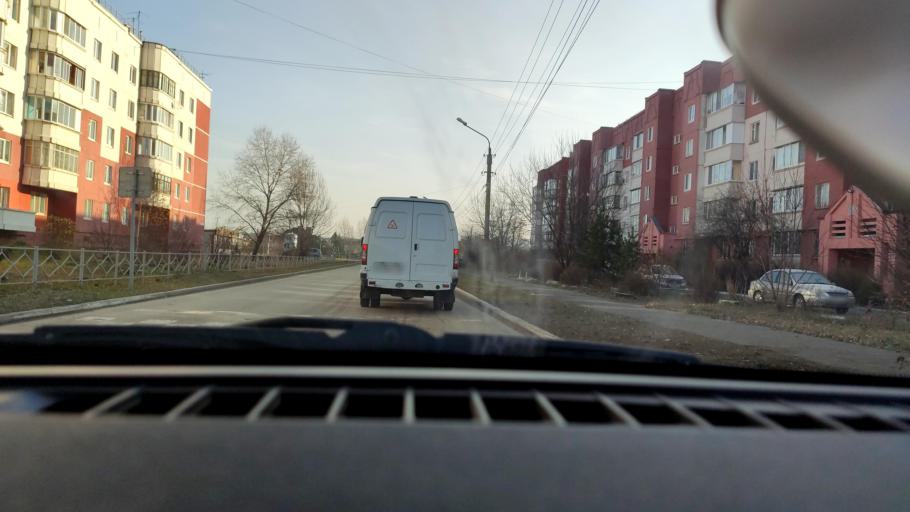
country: RU
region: Perm
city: Kondratovo
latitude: 57.9741
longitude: 56.1087
